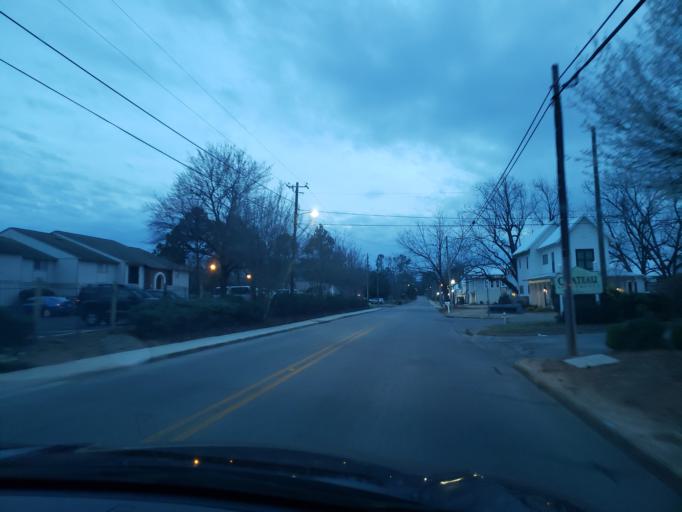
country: US
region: Alabama
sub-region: Lee County
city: Auburn
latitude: 32.6170
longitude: -85.4797
